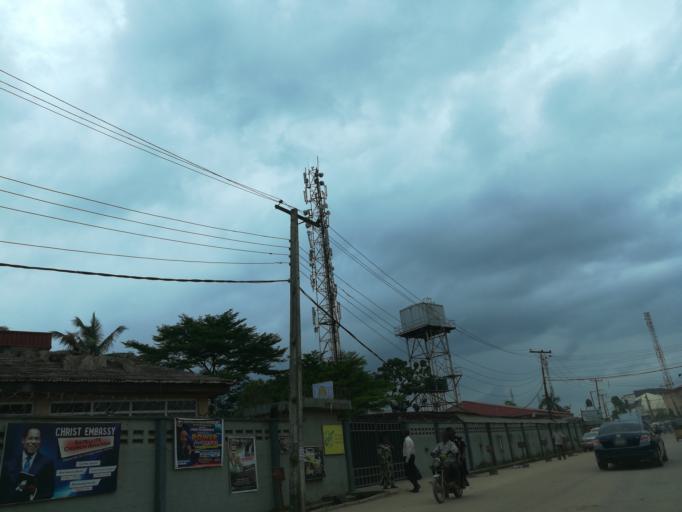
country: NG
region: Lagos
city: Oshodi
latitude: 6.5550
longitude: 3.3286
